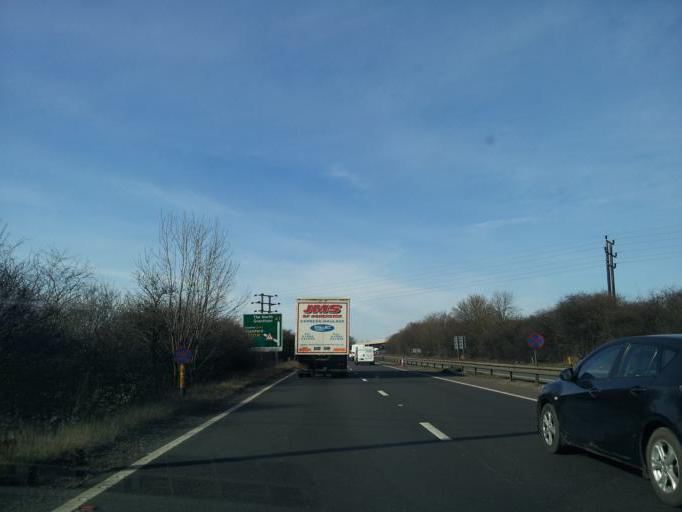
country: GB
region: England
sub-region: District of Rutland
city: Tinwell
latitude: 52.6434
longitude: -0.5013
